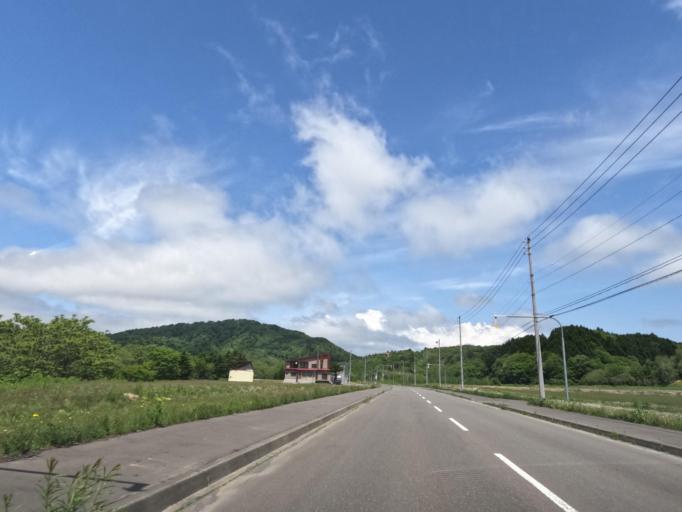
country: JP
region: Hokkaido
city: Tobetsu
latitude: 43.3082
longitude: 141.5559
